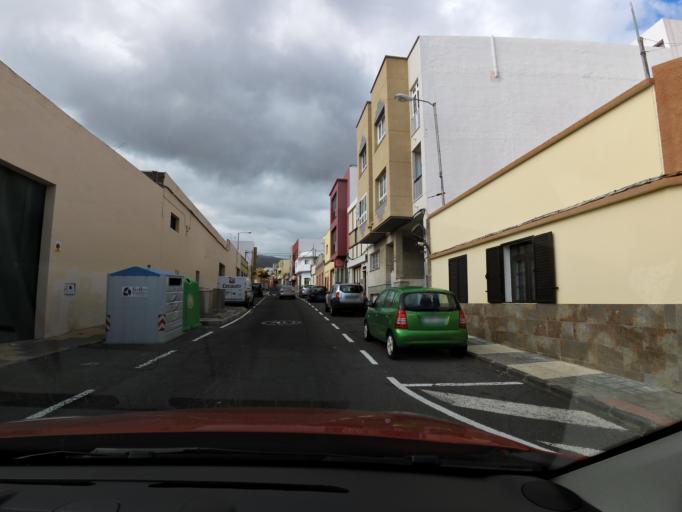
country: ES
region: Canary Islands
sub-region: Provincia de Las Palmas
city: Ingenio
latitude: 27.9191
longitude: -15.4344
